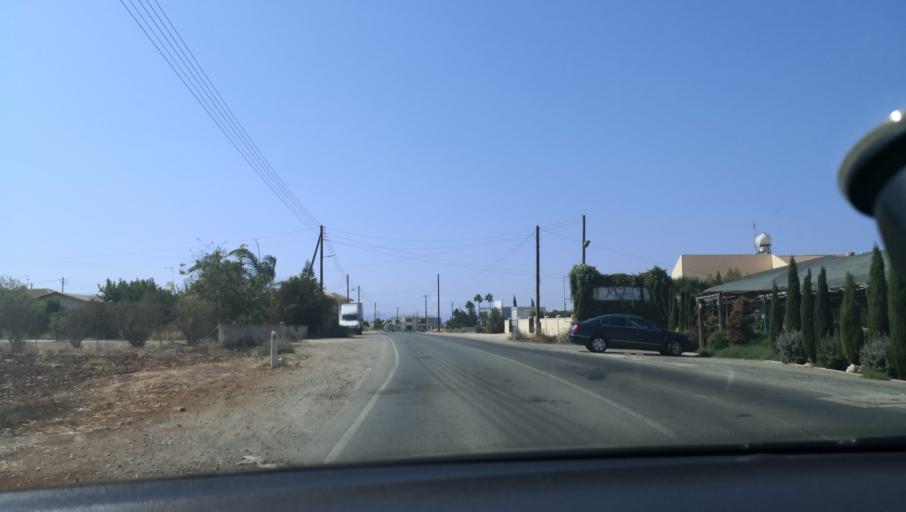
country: CY
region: Lefkosia
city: Kokkinotrimithia
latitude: 35.1154
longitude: 33.2213
